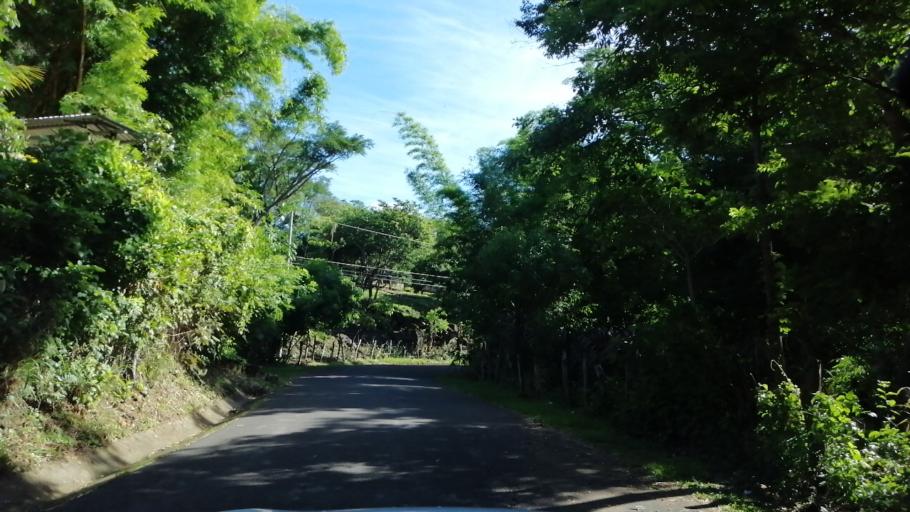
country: SV
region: Morazan
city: Corinto
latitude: 13.8106
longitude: -88.0005
